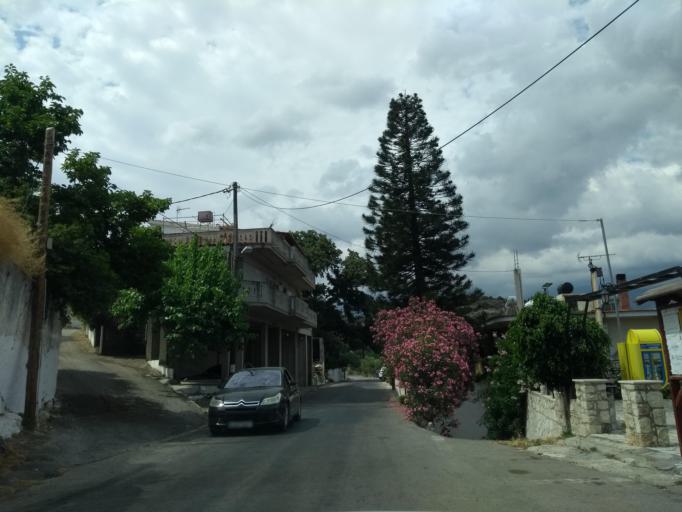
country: GR
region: Crete
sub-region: Nomos Chanias
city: Kalivai
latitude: 35.4363
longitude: 24.1779
